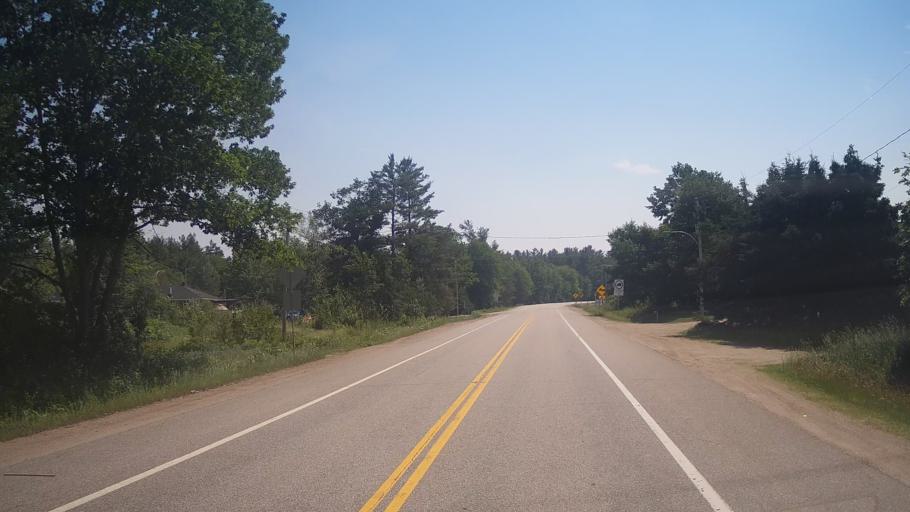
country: CA
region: Quebec
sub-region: Outaouais
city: Fort-Coulonge
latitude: 45.9098
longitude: -76.9209
